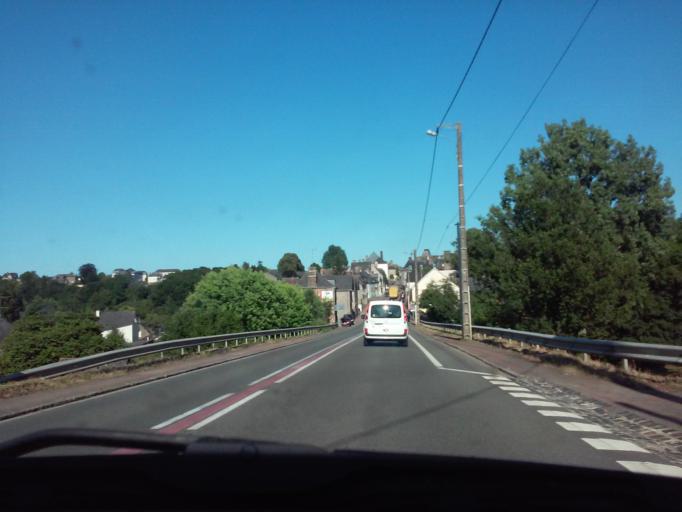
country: FR
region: Pays de la Loire
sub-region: Departement de la Mayenne
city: Ernee
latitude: 48.2971
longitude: -0.9456
